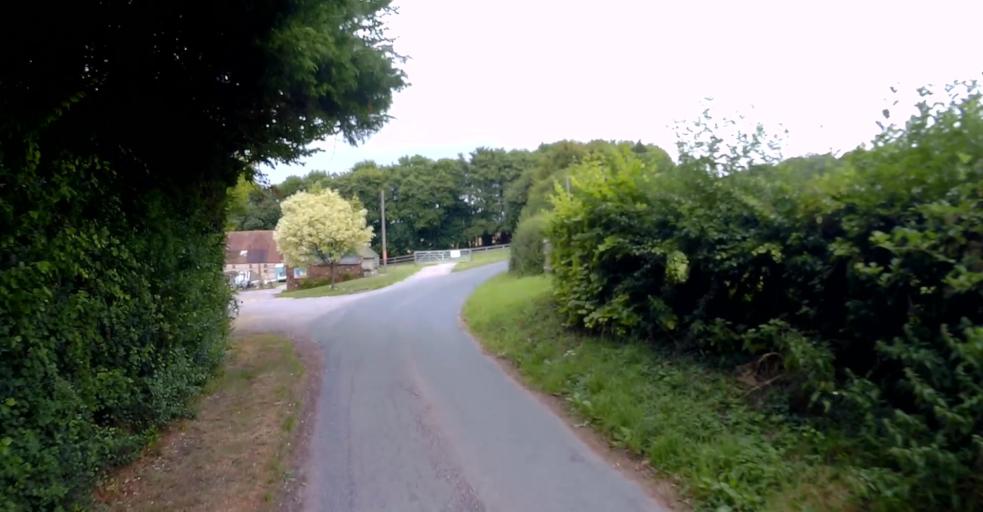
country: GB
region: England
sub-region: Hampshire
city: Kings Worthy
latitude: 51.0553
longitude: -1.2097
